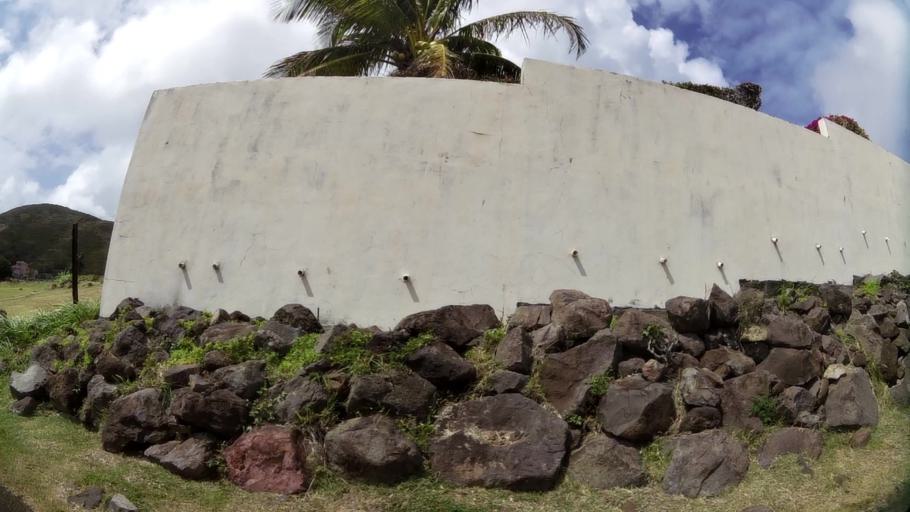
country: KN
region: Saint Peter Basseterre
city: Monkey Hill
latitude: 17.2948
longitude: -62.6943
